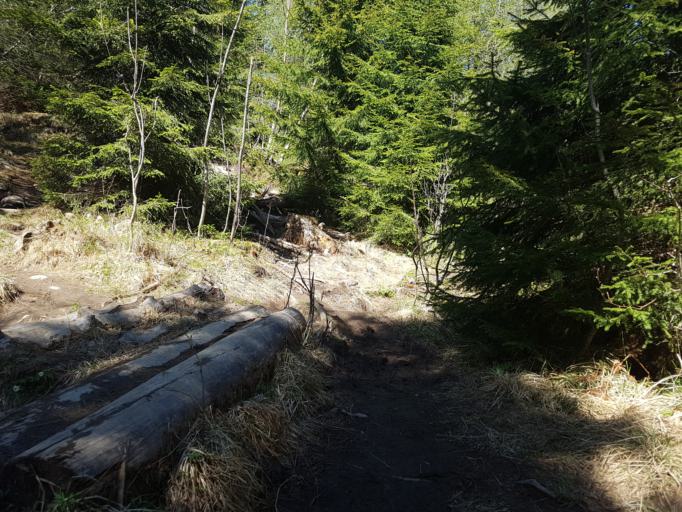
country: NO
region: Sor-Trondelag
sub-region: Trondheim
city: Trondheim
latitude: 63.4354
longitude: 10.3365
